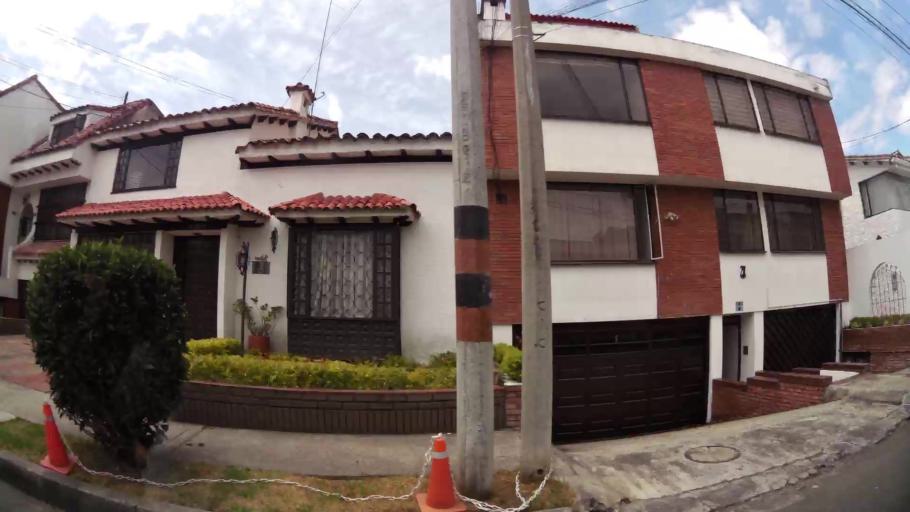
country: CO
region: Bogota D.C.
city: Barrio San Luis
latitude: 4.6985
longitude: -74.0605
